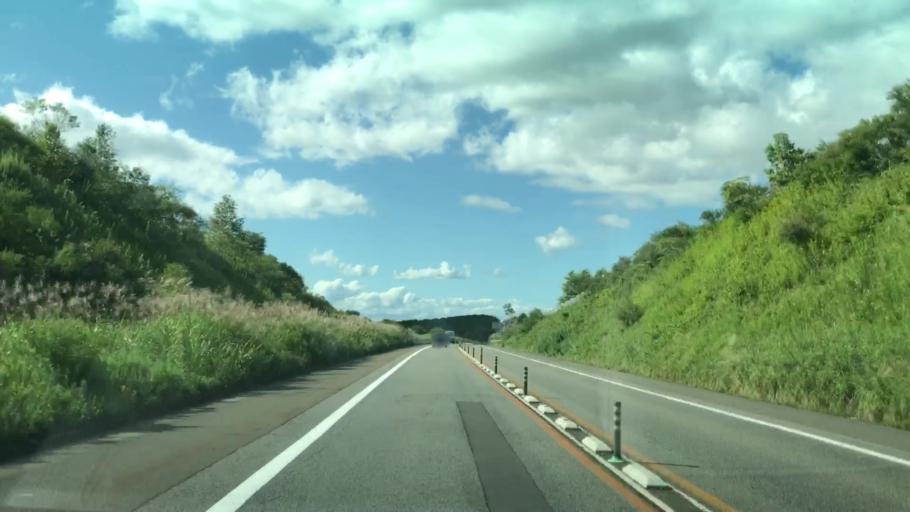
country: JP
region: Hokkaido
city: Muroran
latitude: 42.3975
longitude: 140.9509
